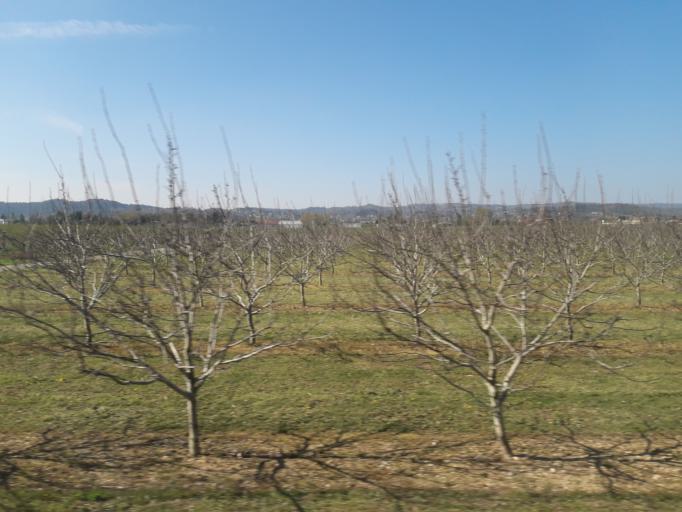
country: FR
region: Rhone-Alpes
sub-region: Departement de la Drome
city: Genissieux
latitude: 45.0600
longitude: 5.1013
